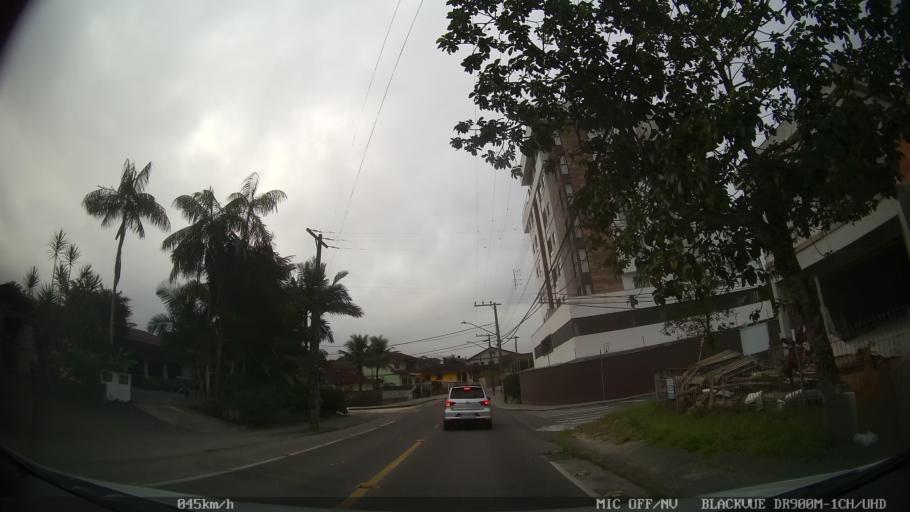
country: BR
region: Santa Catarina
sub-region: Joinville
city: Joinville
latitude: -26.2873
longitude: -48.8723
